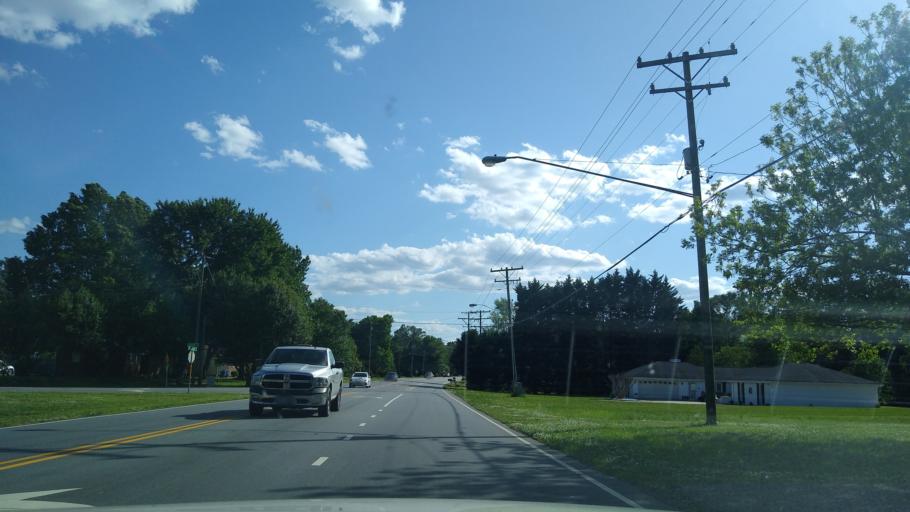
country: US
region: North Carolina
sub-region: Forsyth County
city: Kernersville
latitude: 36.0956
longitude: -80.0876
